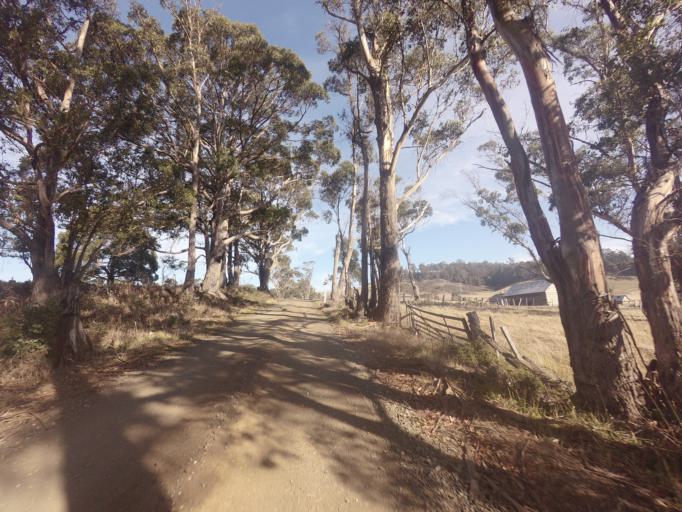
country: AU
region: Tasmania
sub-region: Sorell
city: Sorell
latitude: -42.4801
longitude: 147.4806
